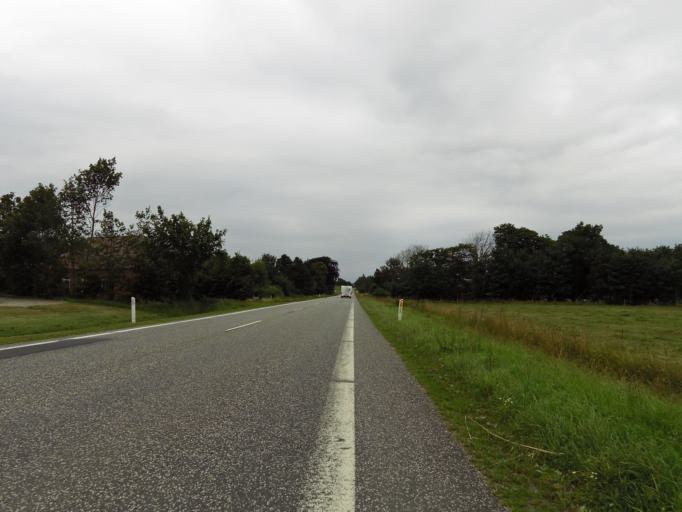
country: DK
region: South Denmark
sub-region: Tonder Kommune
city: Logumkloster
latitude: 55.1150
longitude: 8.9545
